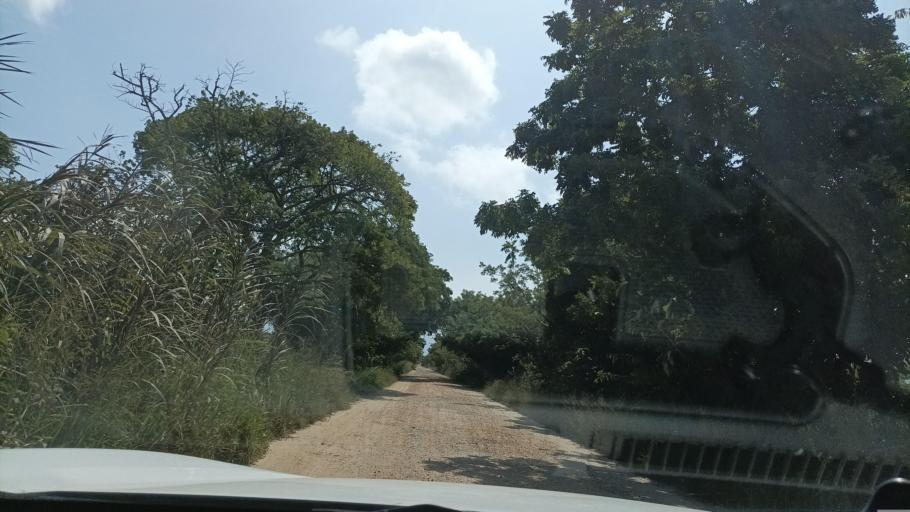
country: MX
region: Veracruz
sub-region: Chinameca
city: Chacalapa
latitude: 18.1321
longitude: -94.6552
